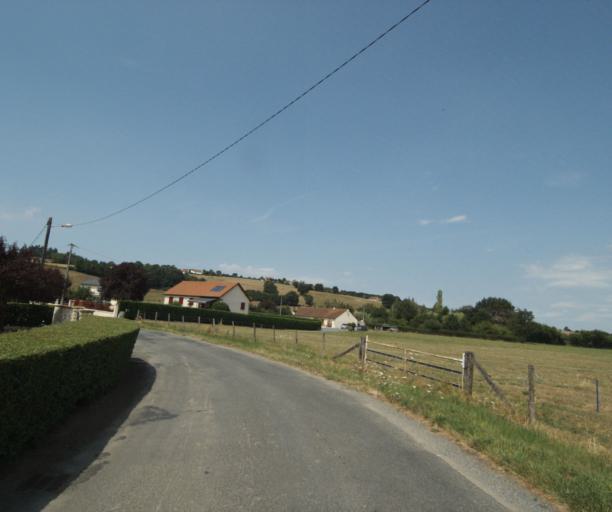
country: FR
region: Bourgogne
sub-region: Departement de Saone-et-Loire
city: Gueugnon
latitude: 46.6115
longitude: 4.0405
